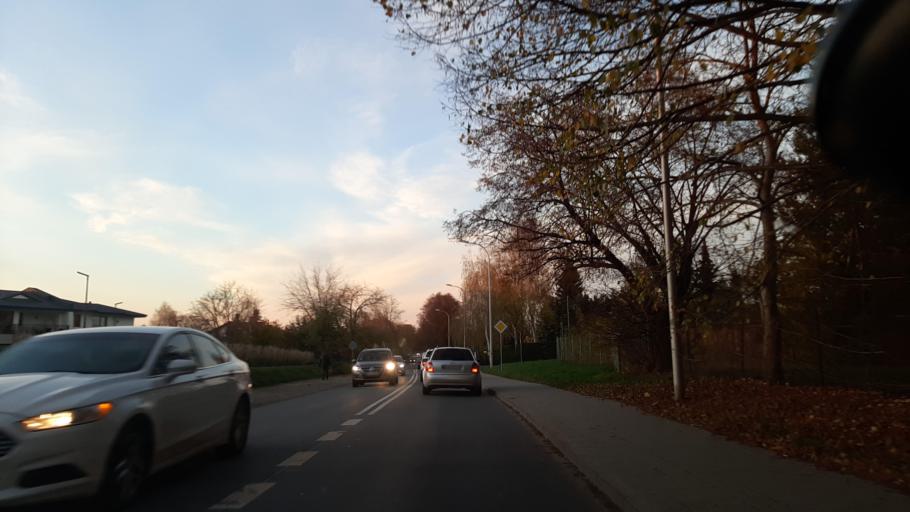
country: PL
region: Lublin Voivodeship
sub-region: Powiat lubelski
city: Lublin
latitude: 51.2807
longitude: 22.5036
